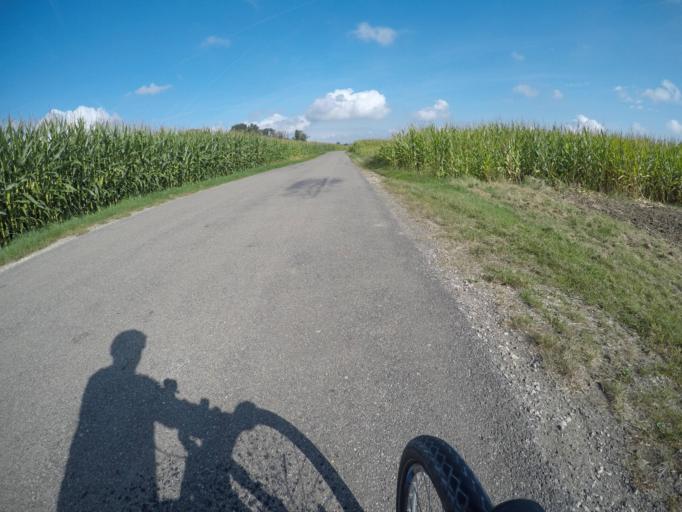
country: DE
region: Bavaria
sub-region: Swabia
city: Buttenwiesen
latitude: 48.6472
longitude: 10.7332
